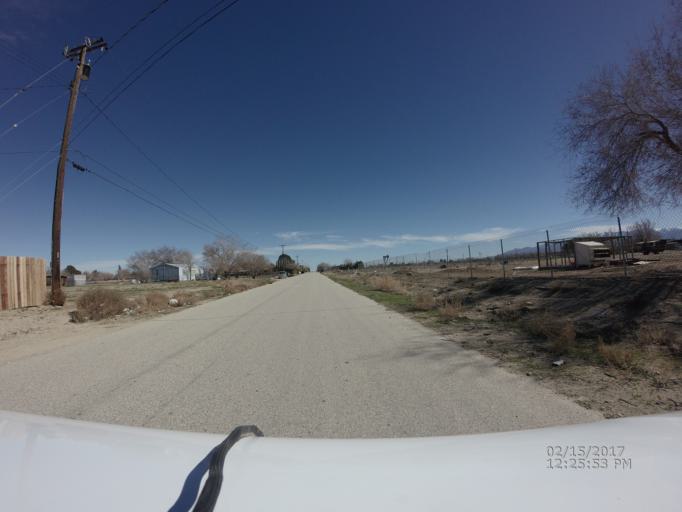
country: US
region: California
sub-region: Los Angeles County
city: Littlerock
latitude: 34.5817
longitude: -117.9600
